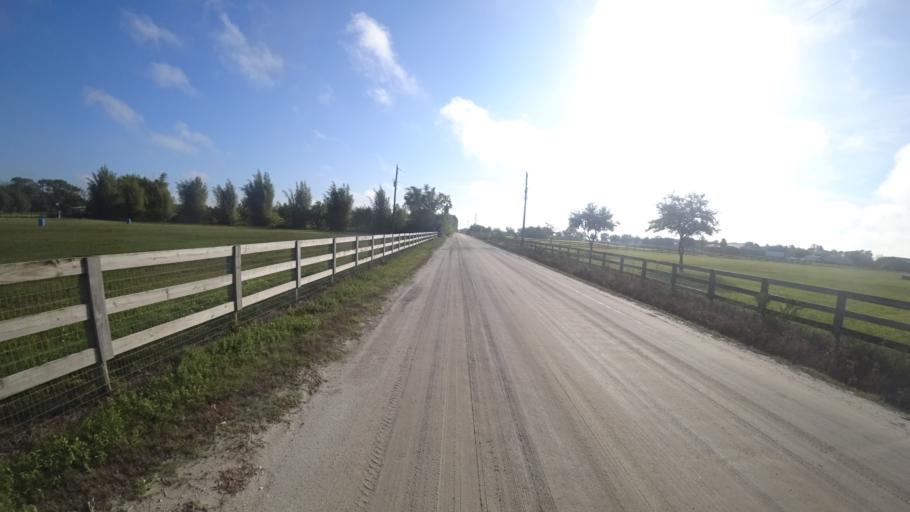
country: US
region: Florida
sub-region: Sarasota County
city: The Meadows
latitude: 27.4310
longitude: -82.3066
